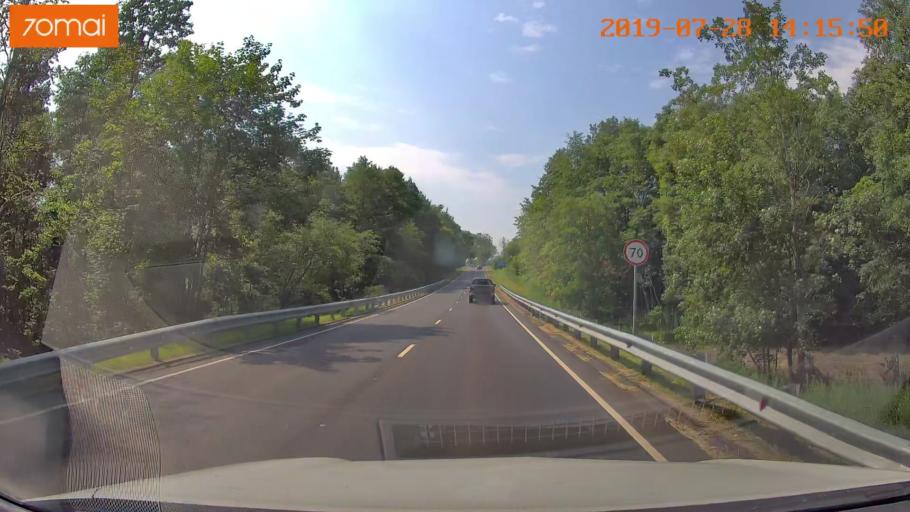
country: RU
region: Kaliningrad
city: Vzmorye
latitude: 54.8170
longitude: 20.2749
